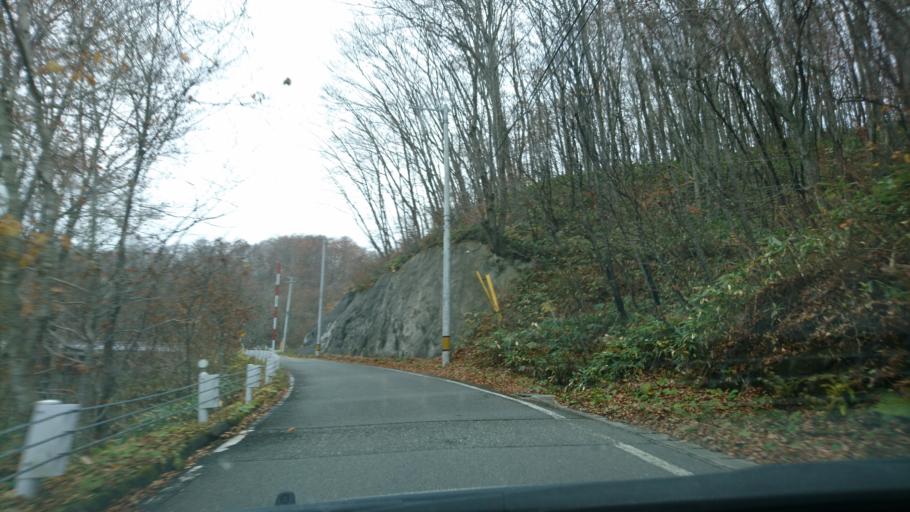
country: JP
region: Iwate
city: Ichinoseki
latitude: 38.9150
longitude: 140.8472
